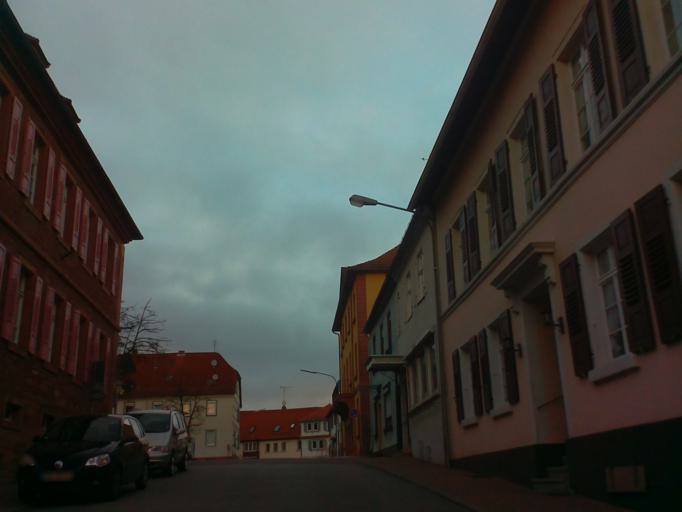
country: DE
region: Hesse
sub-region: Regierungsbezirk Darmstadt
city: Beerfelden
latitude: 49.5679
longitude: 8.9738
